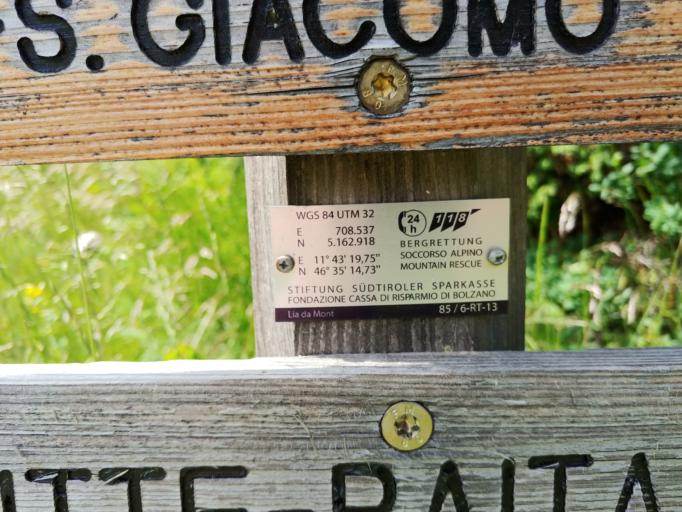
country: IT
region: Trentino-Alto Adige
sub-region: Bolzano
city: Santa Cristina Valgardena
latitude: 46.5875
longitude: 11.7219
